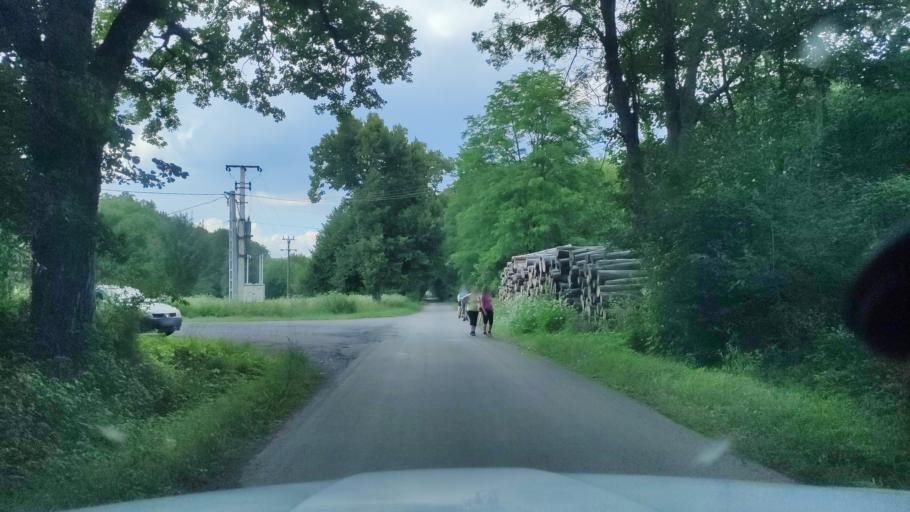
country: HU
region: Heves
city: Parad
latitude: 47.9097
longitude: 20.0568
